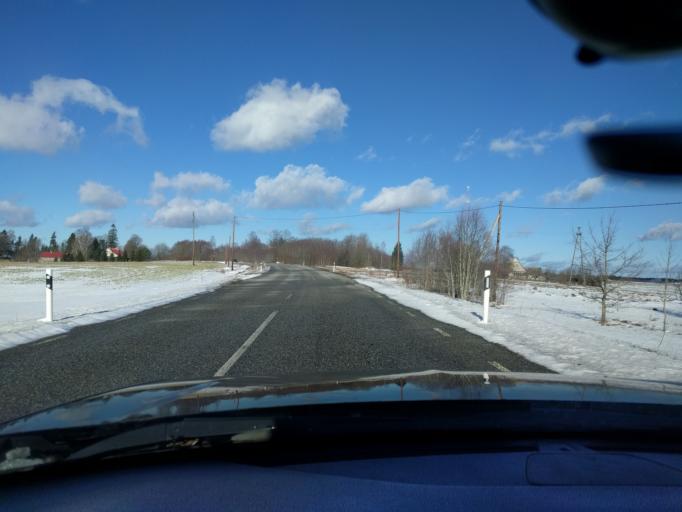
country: EE
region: Harju
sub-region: Raasiku vald
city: Raasiku
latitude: 59.3859
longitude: 25.1955
